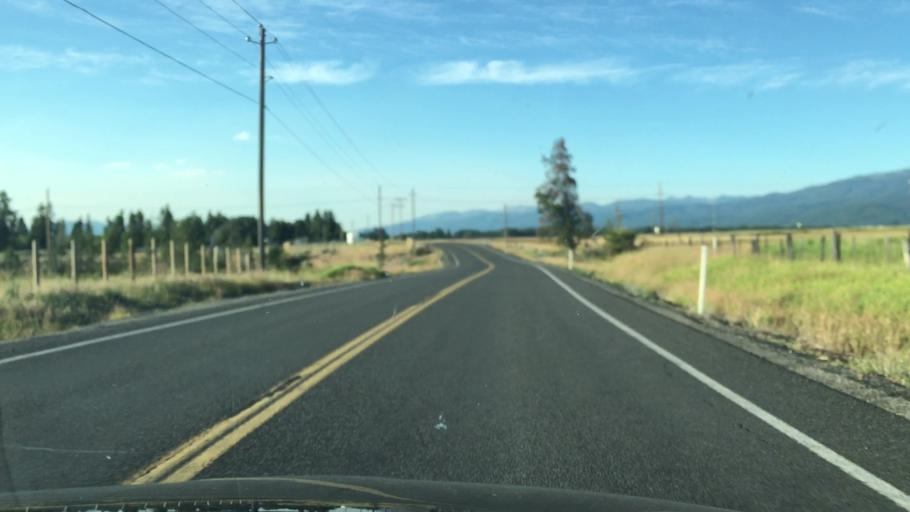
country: US
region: Idaho
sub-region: Valley County
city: McCall
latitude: 44.7723
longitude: -116.0780
